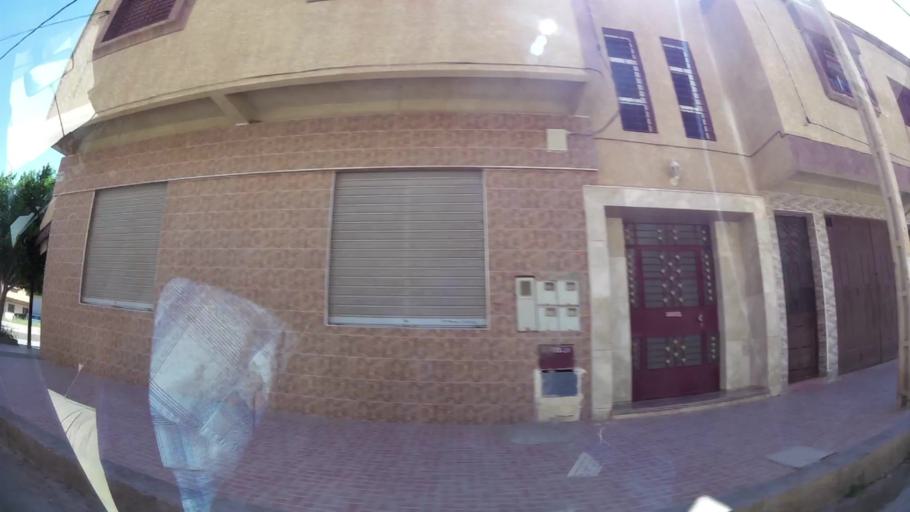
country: MA
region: Oriental
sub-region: Oujda-Angad
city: Oujda
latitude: 34.6875
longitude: -1.9404
